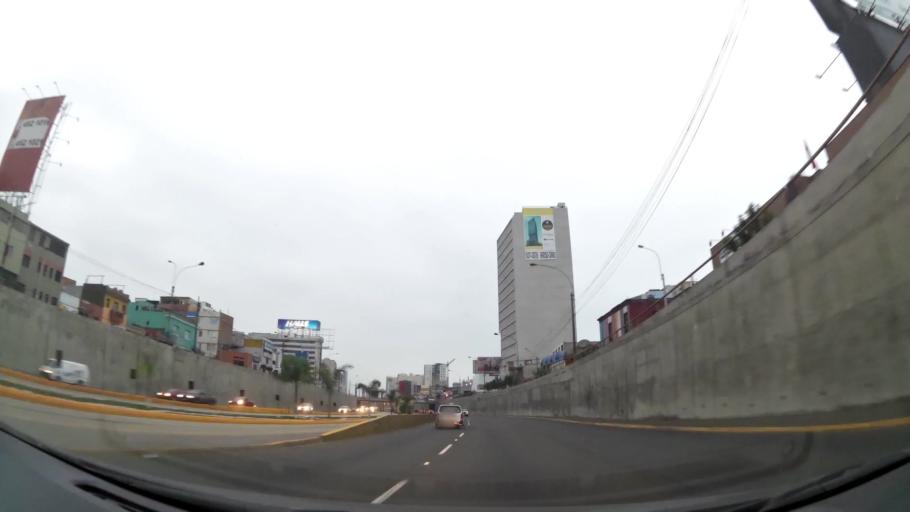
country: PE
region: Lima
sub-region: Lima
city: San Isidro
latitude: -12.1169
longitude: -77.0265
